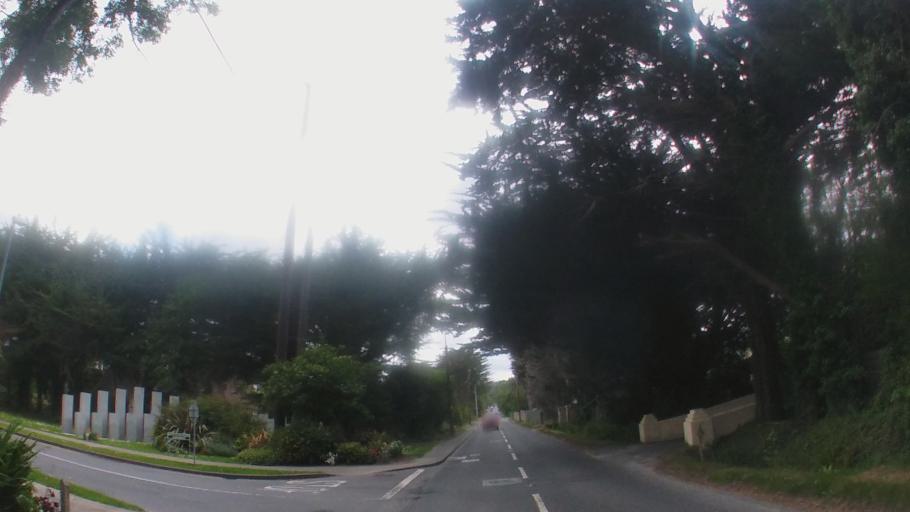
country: IE
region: Leinster
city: Foxrock
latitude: 53.2474
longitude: -6.1833
